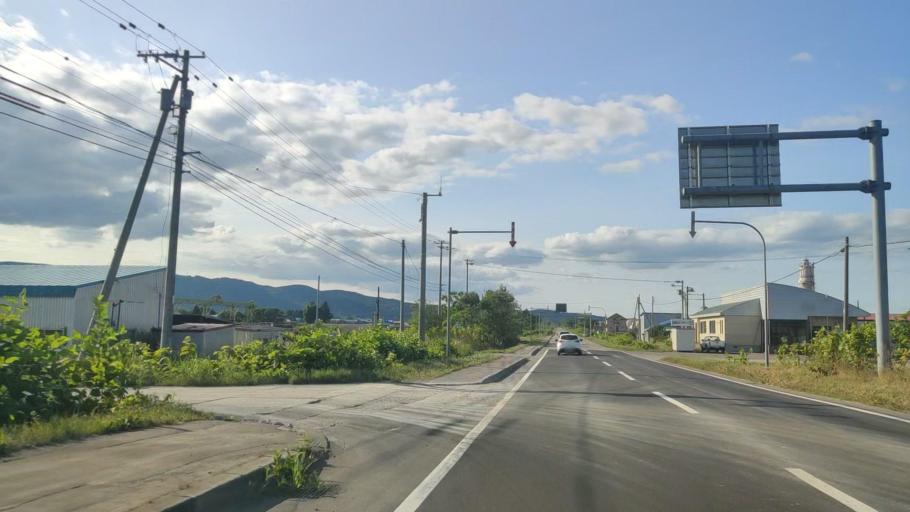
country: JP
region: Hokkaido
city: Makubetsu
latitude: 44.8211
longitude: 142.0671
